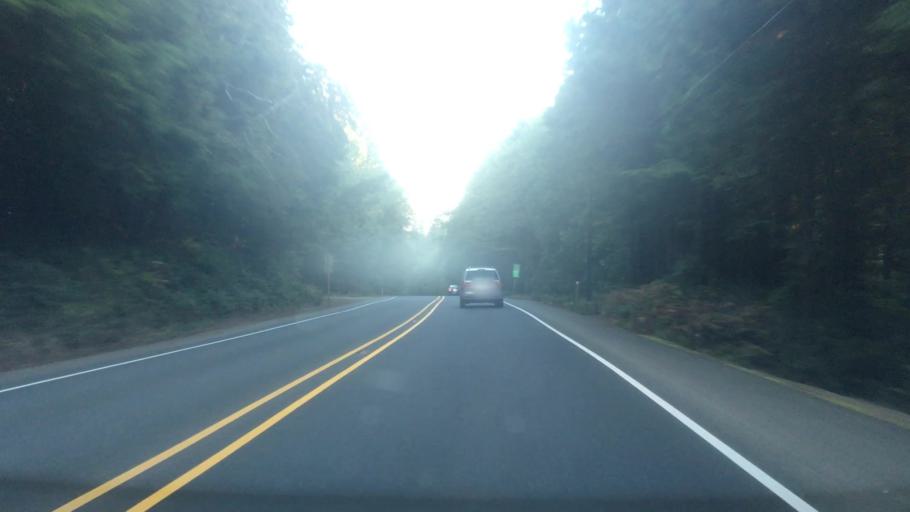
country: US
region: Oregon
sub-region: Clatsop County
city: Cannon Beach
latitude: 45.7814
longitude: -123.9560
